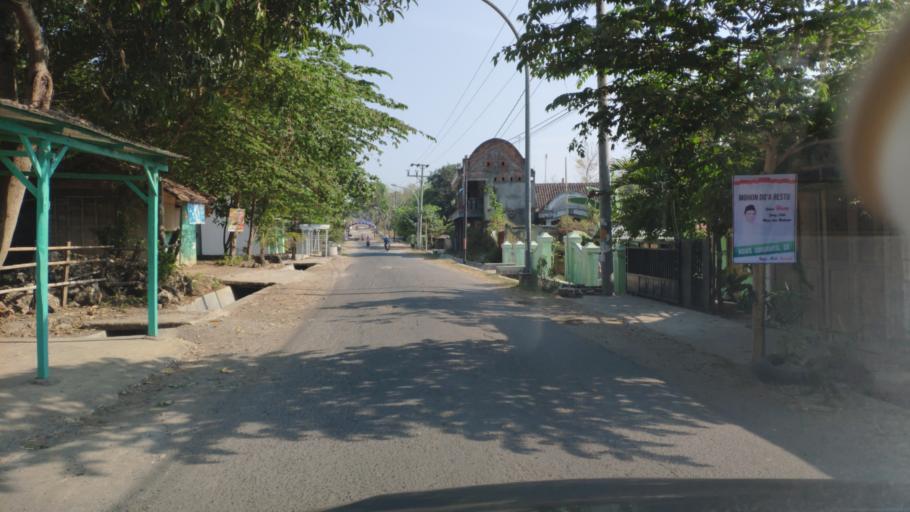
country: ID
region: Central Java
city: Maguwon
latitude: -6.9666
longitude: 111.3801
